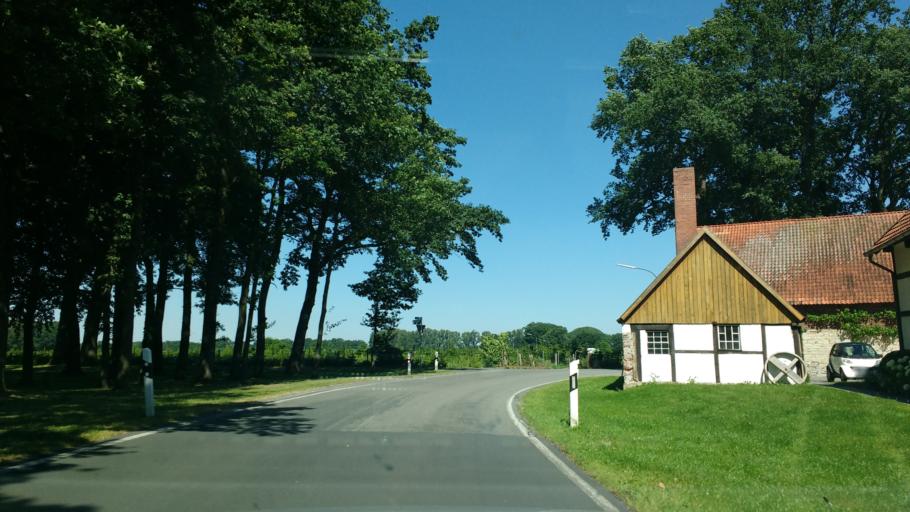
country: DE
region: North Rhine-Westphalia
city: Geseke
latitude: 51.7074
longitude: 8.4574
